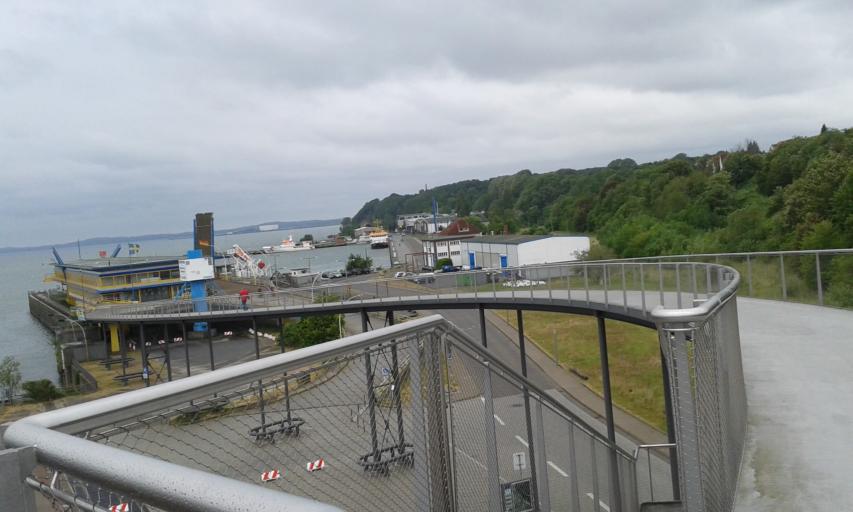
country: DE
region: Mecklenburg-Vorpommern
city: Sassnitz
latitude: 54.5129
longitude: 13.6415
